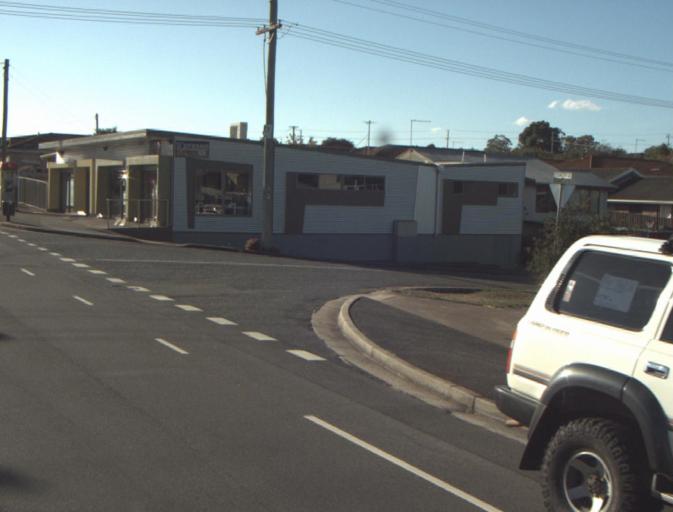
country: AU
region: Tasmania
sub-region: Launceston
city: Summerhill
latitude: -41.4685
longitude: 147.1315
